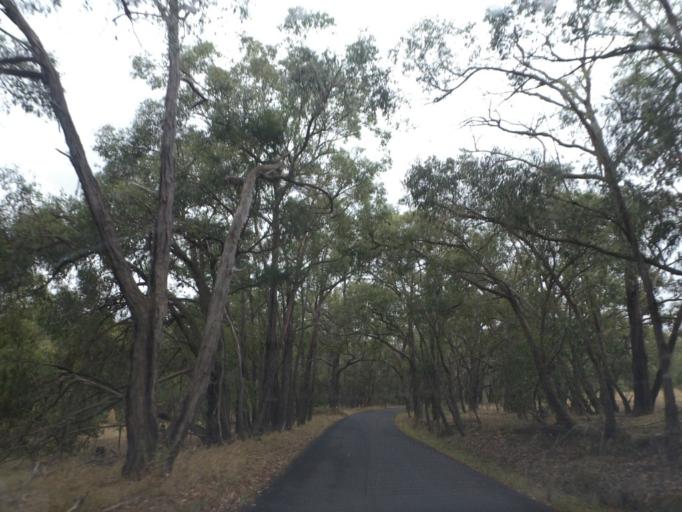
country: AU
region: Victoria
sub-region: Nillumbik
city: Saint Andrews
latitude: -37.6189
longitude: 145.3248
